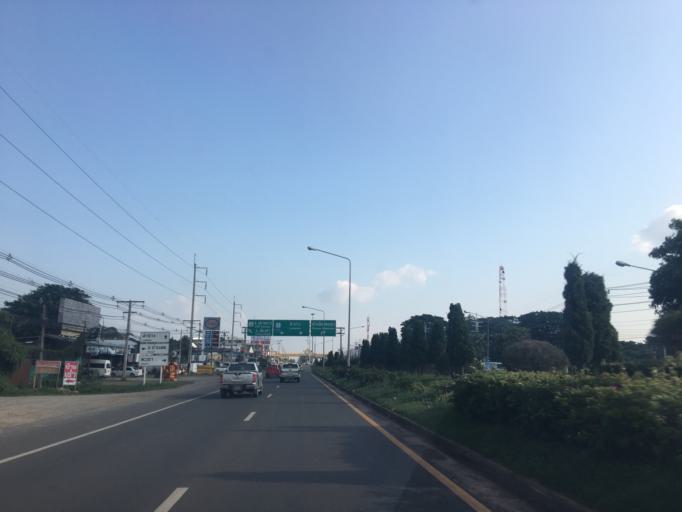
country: TH
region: Phayao
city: Phayao
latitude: 19.1743
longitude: 99.9041
